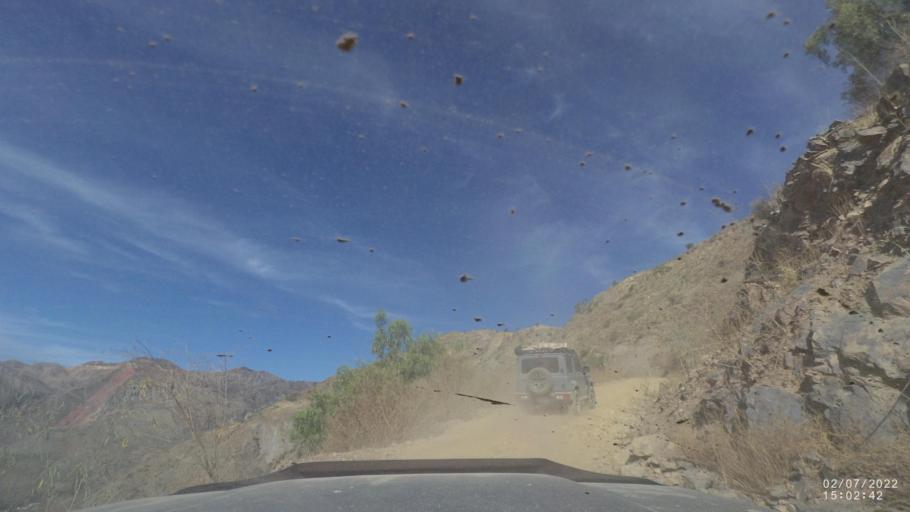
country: BO
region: Cochabamba
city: Irpa Irpa
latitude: -17.8571
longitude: -66.4390
